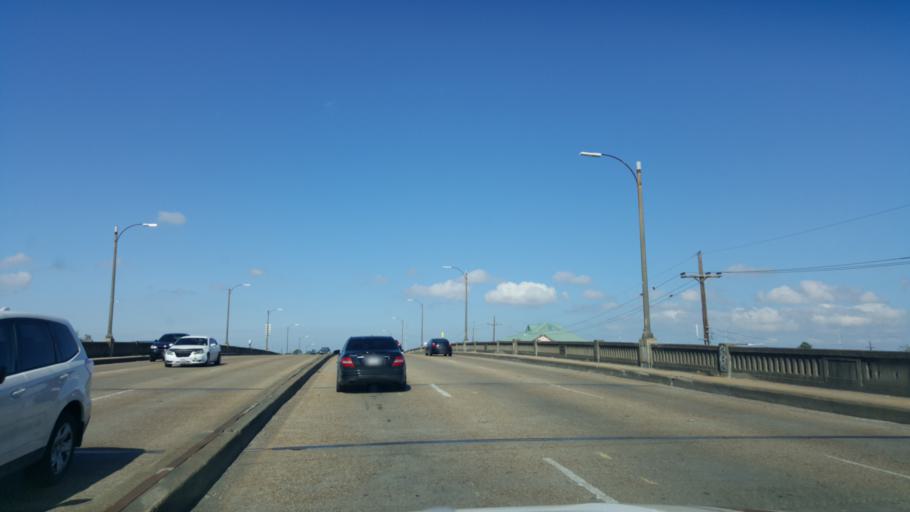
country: US
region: Louisiana
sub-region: Orleans Parish
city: New Orleans
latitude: 29.9847
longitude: -90.0581
